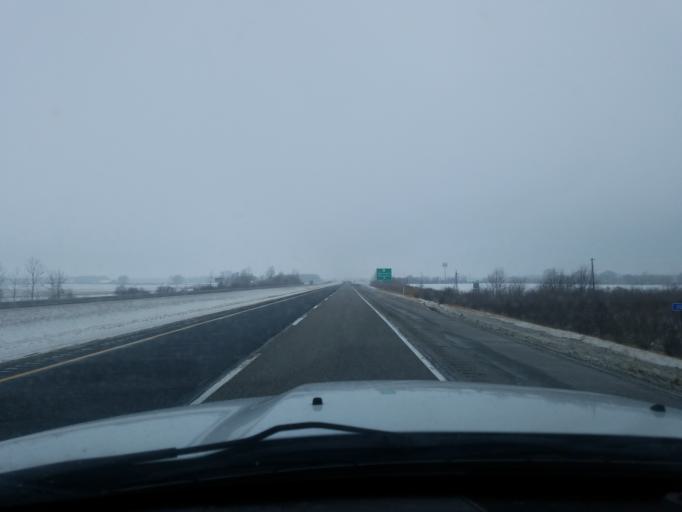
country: US
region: Indiana
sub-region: Fulton County
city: Rochester
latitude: 41.0435
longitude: -86.2085
